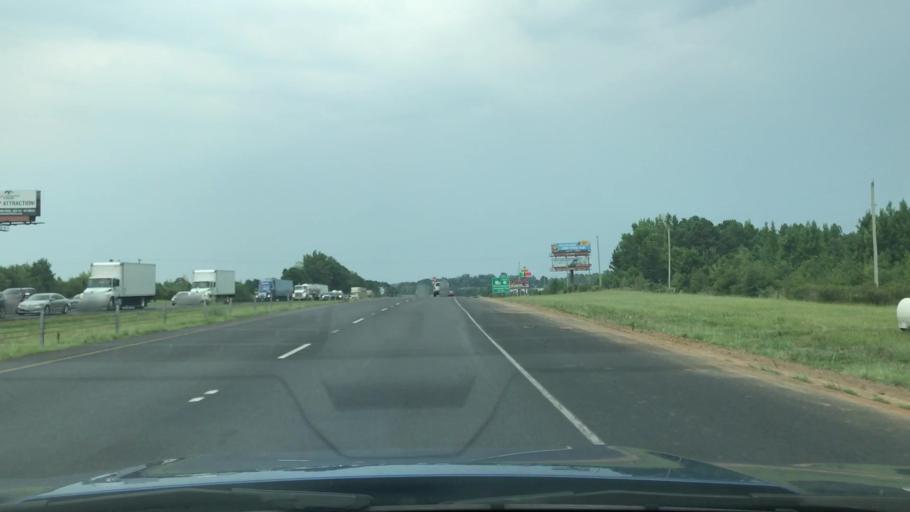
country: US
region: Louisiana
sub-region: Caddo Parish
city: Greenwood
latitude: 32.4501
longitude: -93.9919
